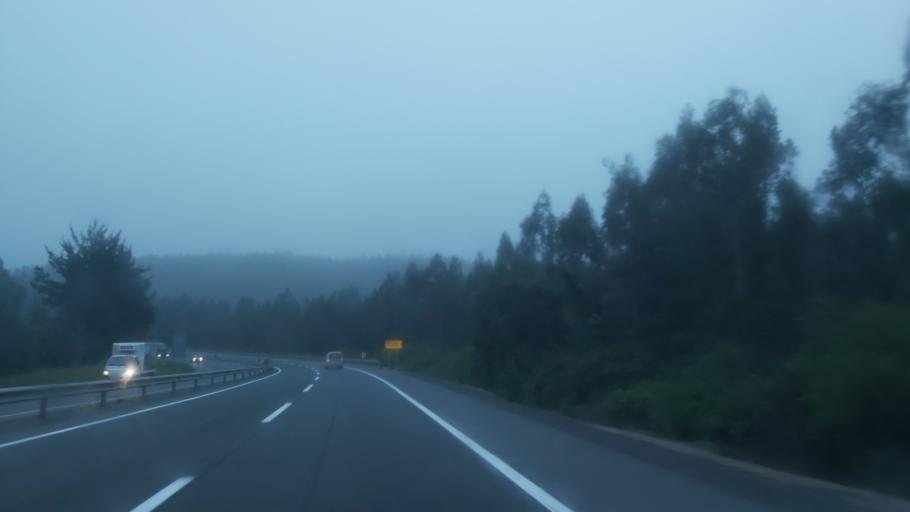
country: CL
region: Biobio
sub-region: Provincia de Concepcion
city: Penco
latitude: -36.7384
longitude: -72.8980
